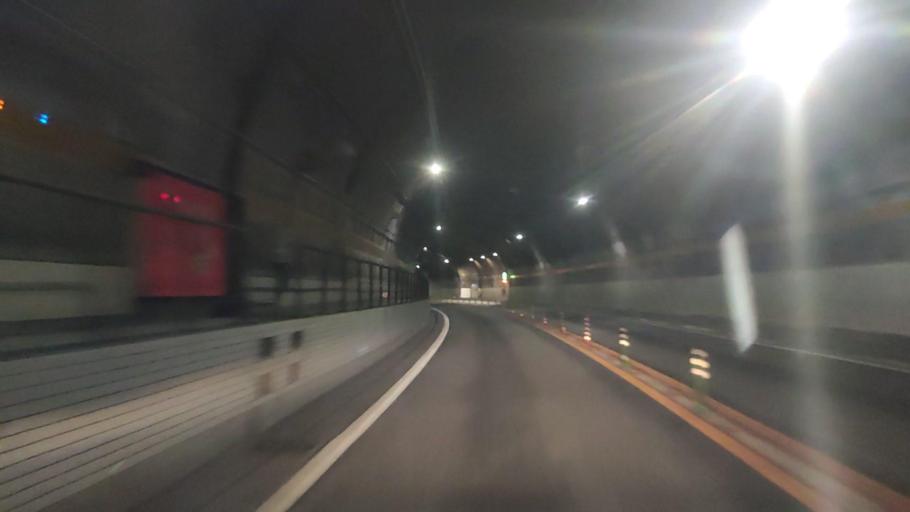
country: JP
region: Nagasaki
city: Obita
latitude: 32.7903
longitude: 129.8813
